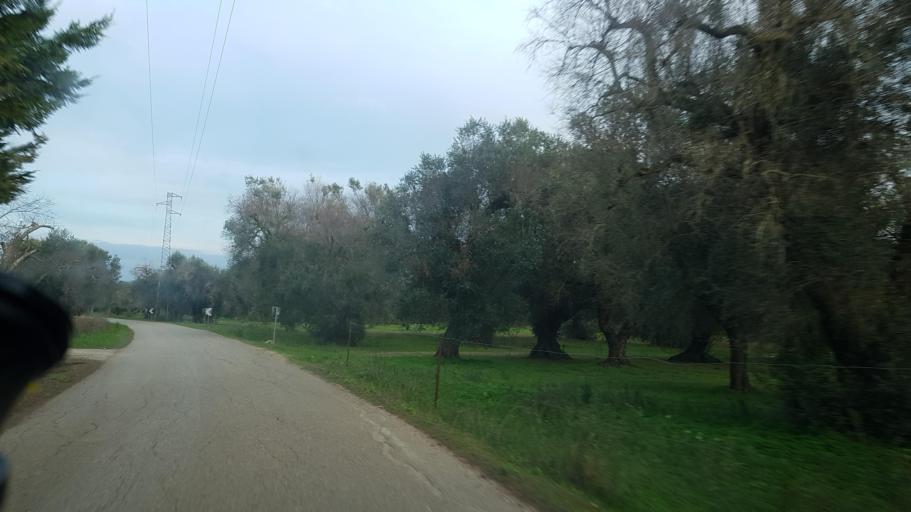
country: IT
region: Apulia
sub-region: Provincia di Brindisi
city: Latiano
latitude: 40.5376
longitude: 17.7541
